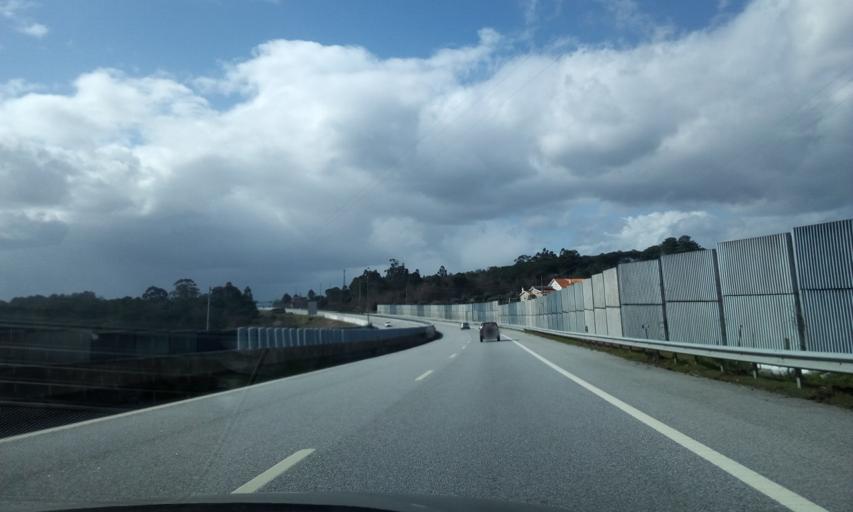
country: PT
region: Viseu
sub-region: Mangualde
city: Mangualde
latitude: 40.6226
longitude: -7.7705
